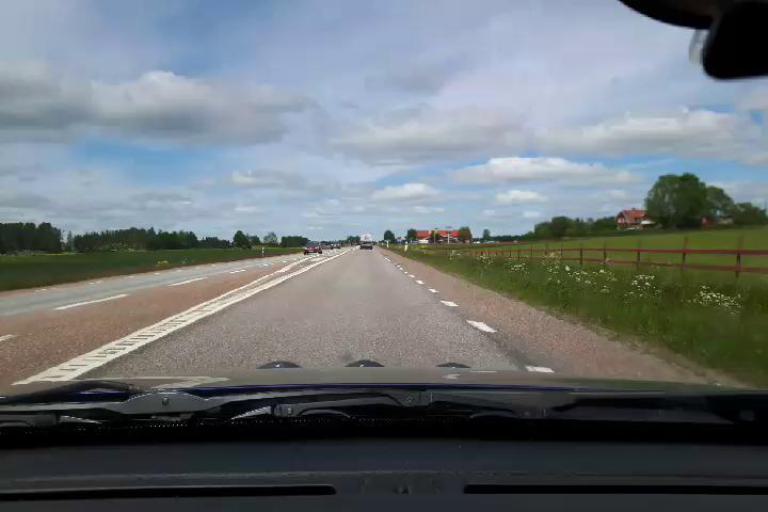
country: SE
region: Uppsala
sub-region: Uppsala Kommun
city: Gamla Uppsala
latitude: 59.9352
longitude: 17.5955
